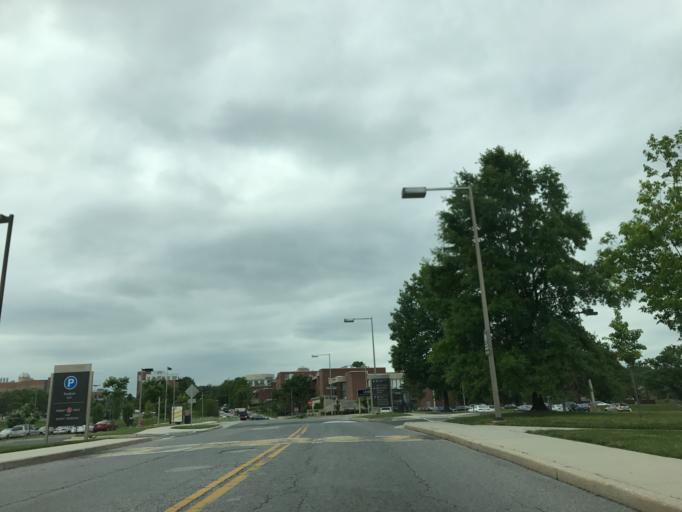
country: US
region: Maryland
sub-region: Baltimore County
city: Arbutus
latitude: 39.2540
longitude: -76.7048
